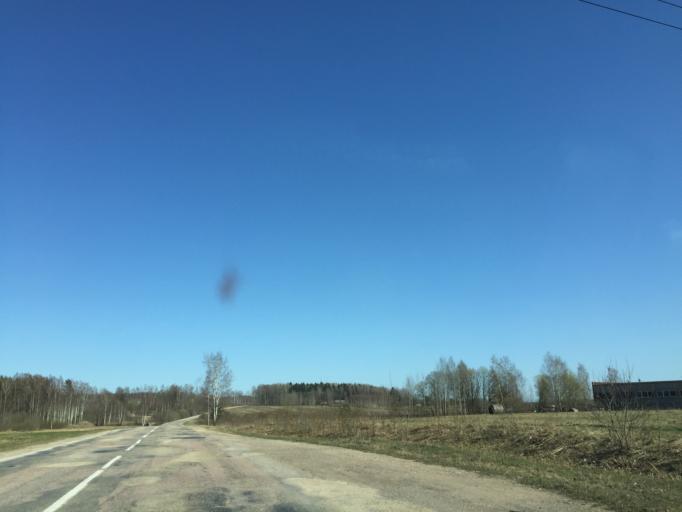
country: LV
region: Malpils
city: Malpils
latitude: 57.0228
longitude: 24.9531
